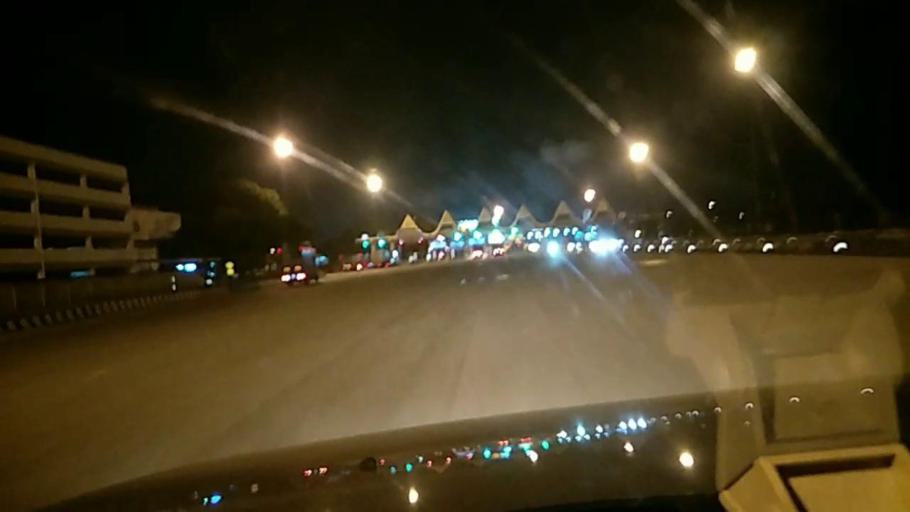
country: MY
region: Penang
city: Juru
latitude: 5.3220
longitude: 100.4368
